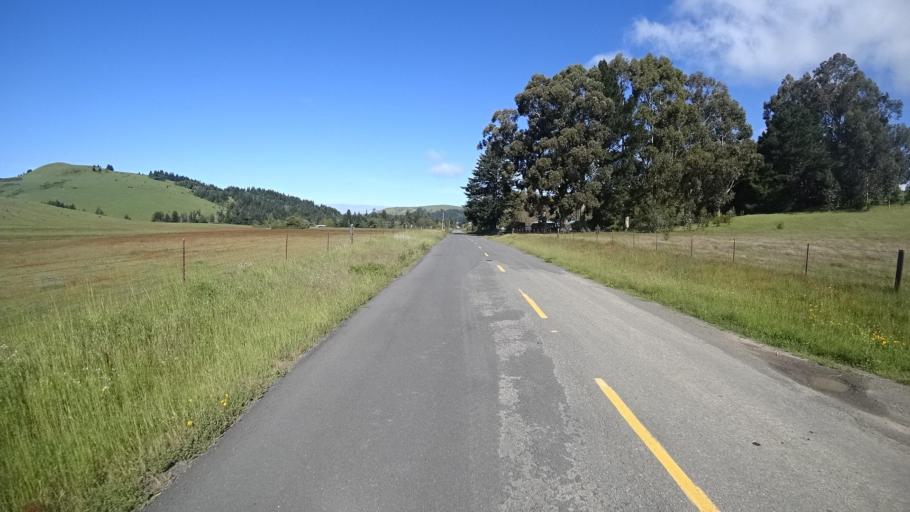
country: US
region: California
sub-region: Humboldt County
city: Ferndale
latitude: 40.3384
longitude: -124.3123
